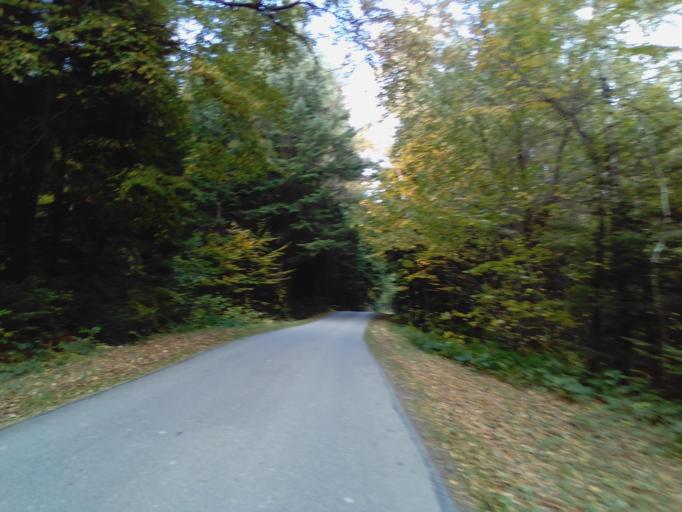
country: PL
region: Subcarpathian Voivodeship
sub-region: Powiat strzyzowski
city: Konieczkowa
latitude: 49.8536
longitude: 21.9605
